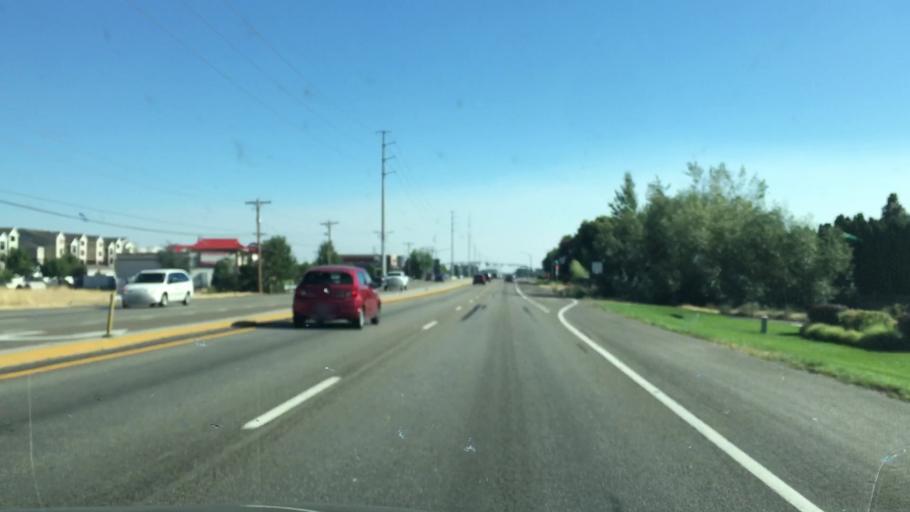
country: US
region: Idaho
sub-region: Ada County
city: Meridian
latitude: 43.6300
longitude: -116.3546
